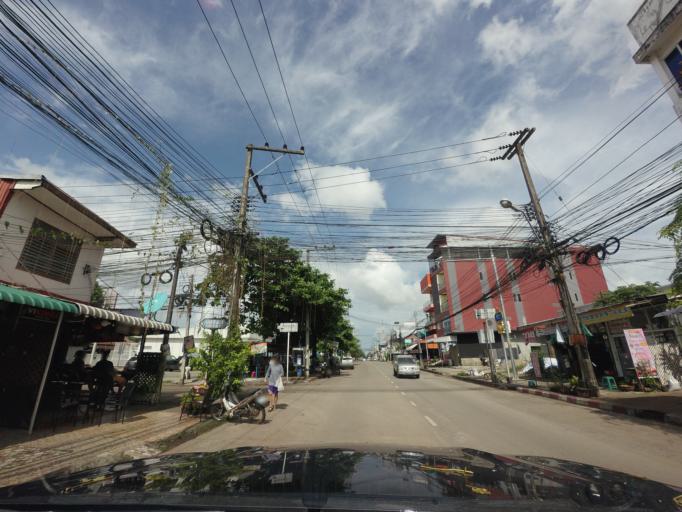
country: TH
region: Changwat Udon Thani
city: Udon Thani
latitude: 17.4074
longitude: 102.8029
